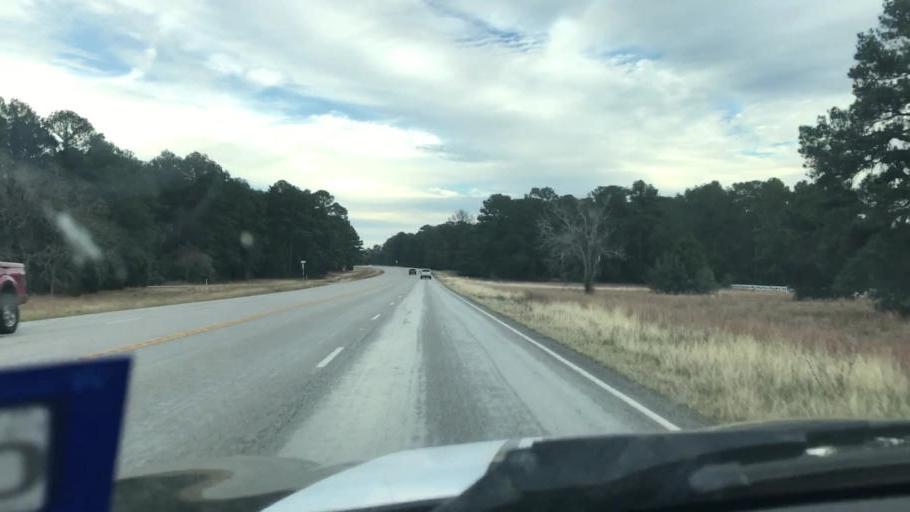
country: US
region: Texas
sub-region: Bastrop County
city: Camp Swift
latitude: 30.2434
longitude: -97.2163
